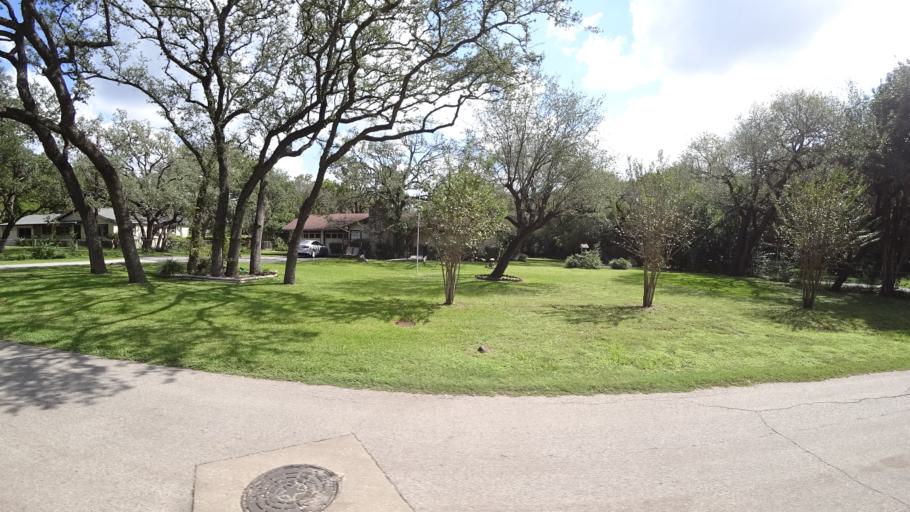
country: US
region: Texas
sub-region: Travis County
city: Onion Creek
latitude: 30.1917
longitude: -97.8018
